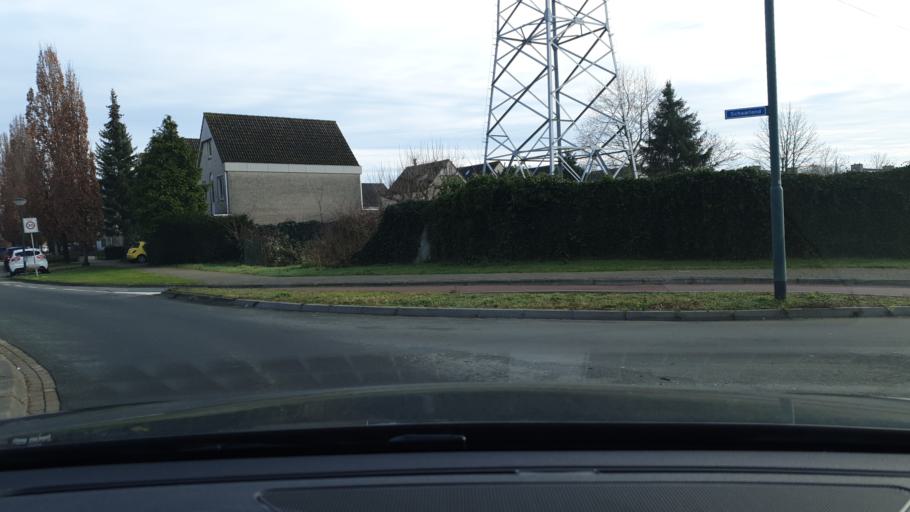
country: NL
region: North Brabant
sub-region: Gemeente Geldrop-Mierlo
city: Geldrop
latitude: 51.4242
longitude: 5.5364
